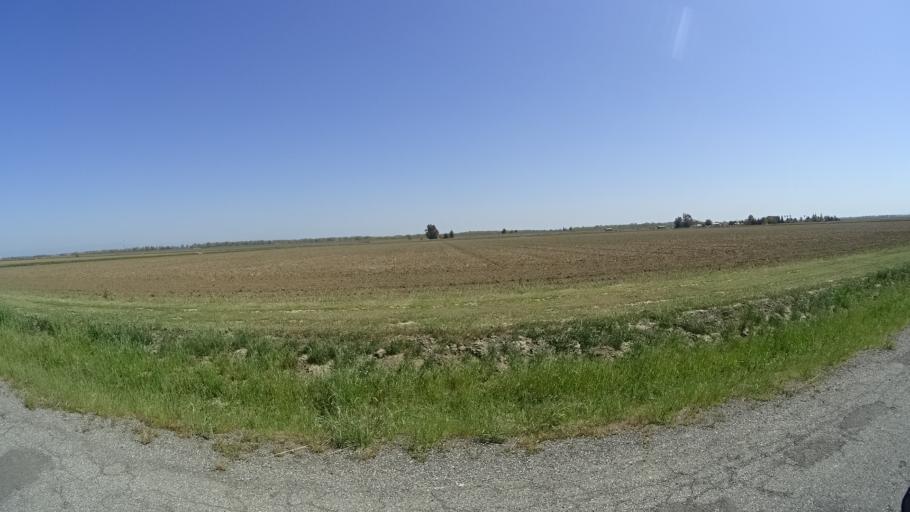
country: US
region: California
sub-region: Glenn County
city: Hamilton City
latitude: 39.5713
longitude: -122.0278
